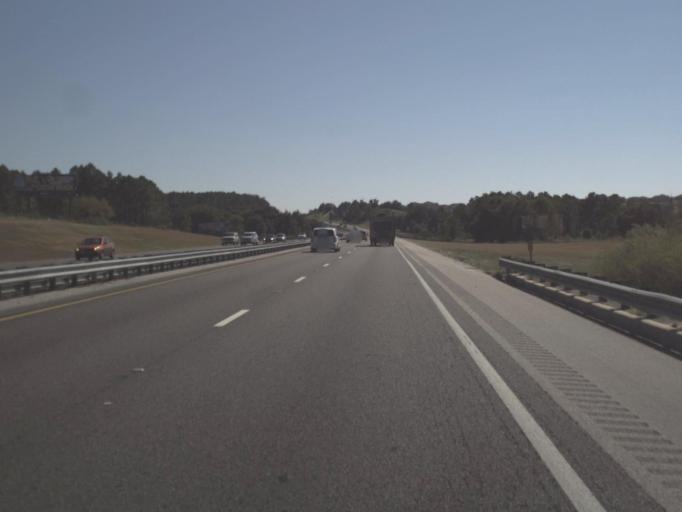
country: US
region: Florida
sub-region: Lake County
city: Montverde
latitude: 28.5788
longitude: -81.7026
